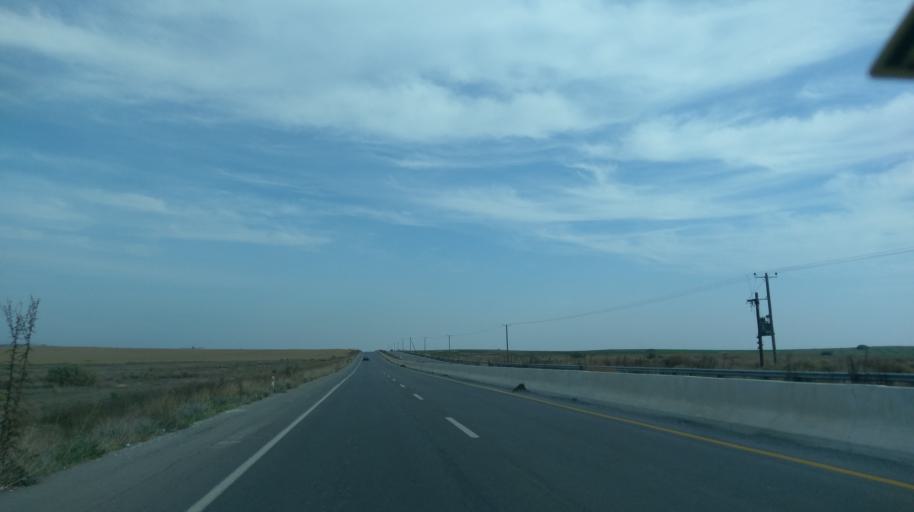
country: CY
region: Lefkosia
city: Mammari
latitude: 35.2133
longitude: 33.1979
